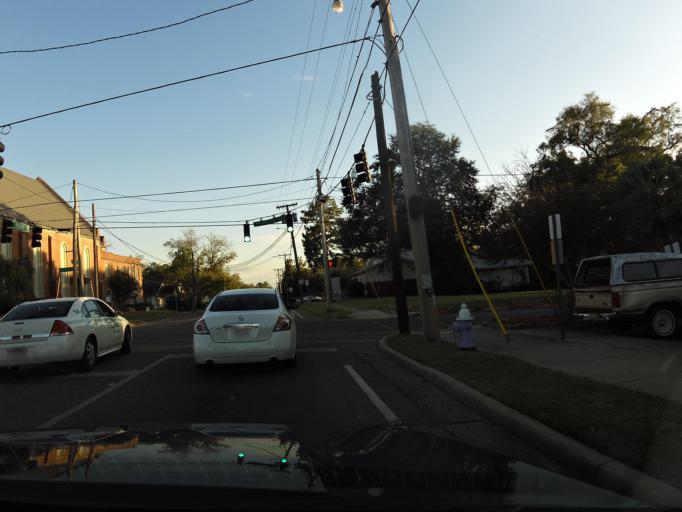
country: US
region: Alabama
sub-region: Houston County
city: Dothan
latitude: 31.2195
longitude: -85.3902
